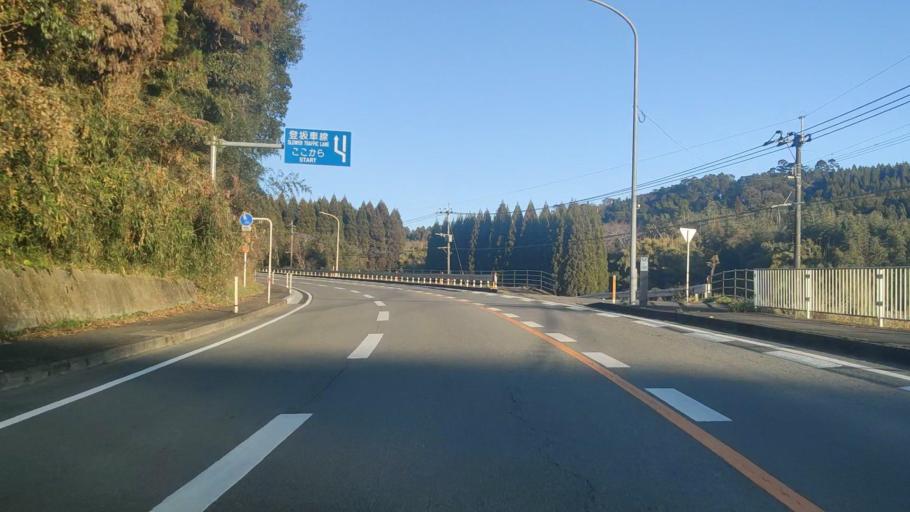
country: JP
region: Miyazaki
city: Takanabe
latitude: 32.1502
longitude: 131.5249
